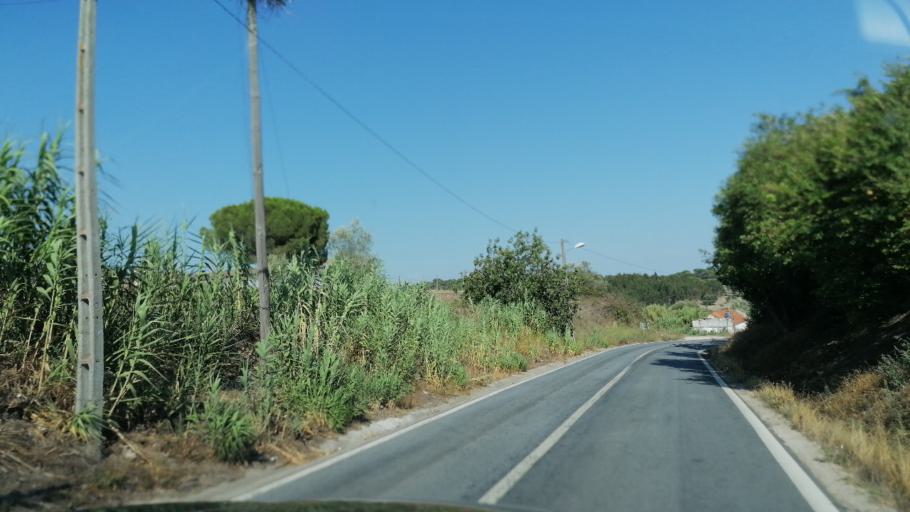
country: PT
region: Santarem
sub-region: Benavente
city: Poceirao
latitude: 38.7689
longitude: -8.6248
